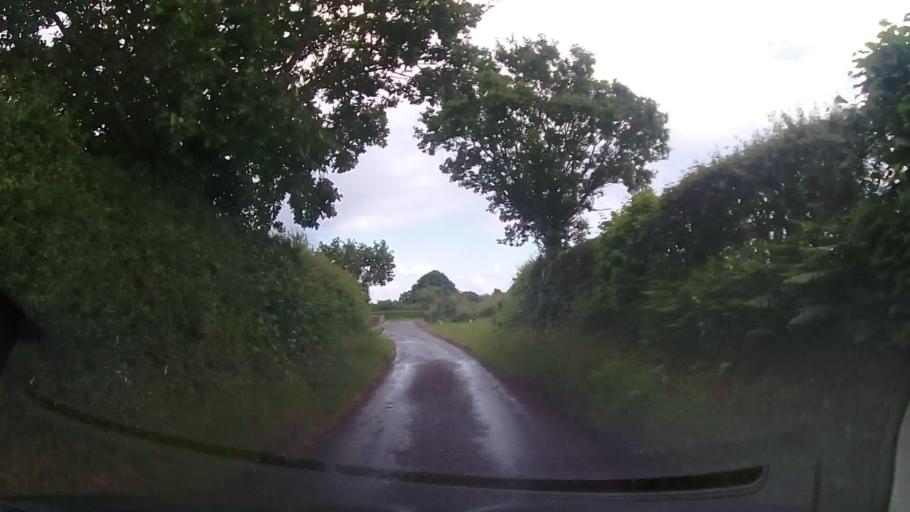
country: GB
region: England
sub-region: Telford and Wrekin
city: Ironbridge
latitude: 52.6488
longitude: -2.5099
